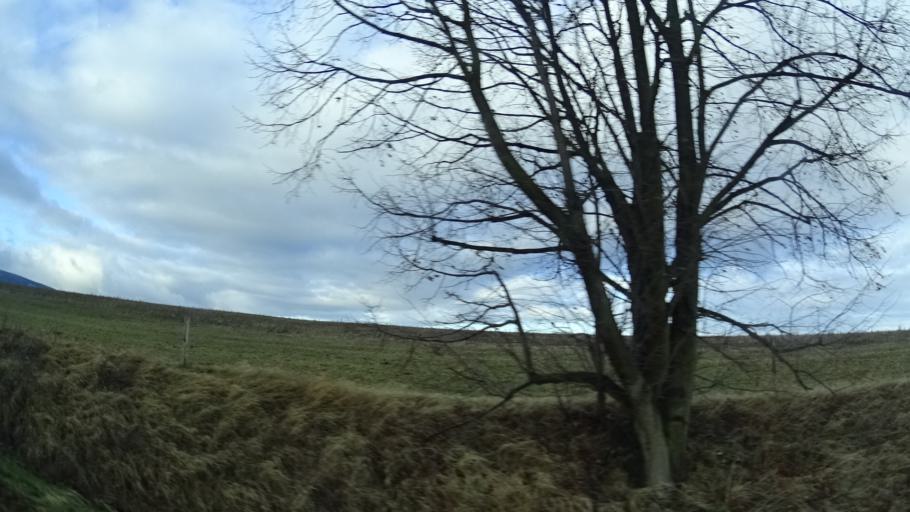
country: DE
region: Thuringia
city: Crawinkel
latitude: 50.7867
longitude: 10.8132
